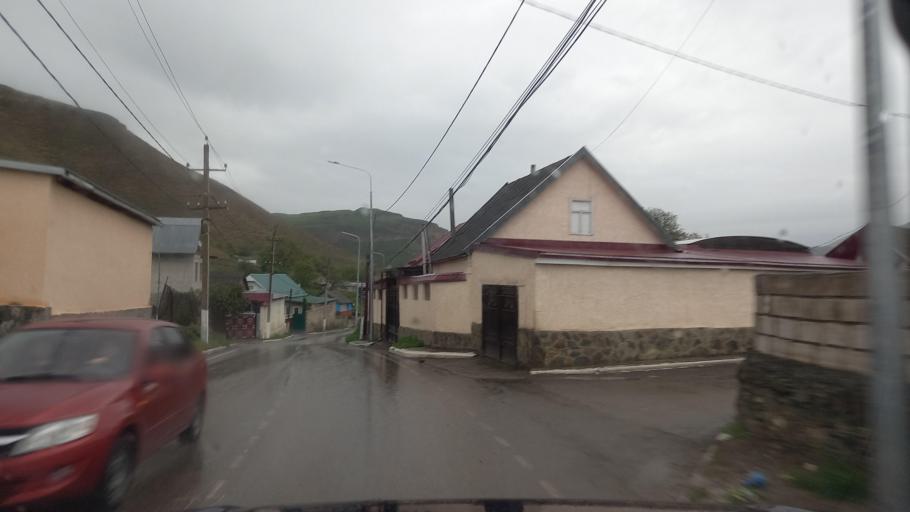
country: RU
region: Kabardino-Balkariya
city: Gundelen
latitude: 43.5993
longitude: 43.1562
